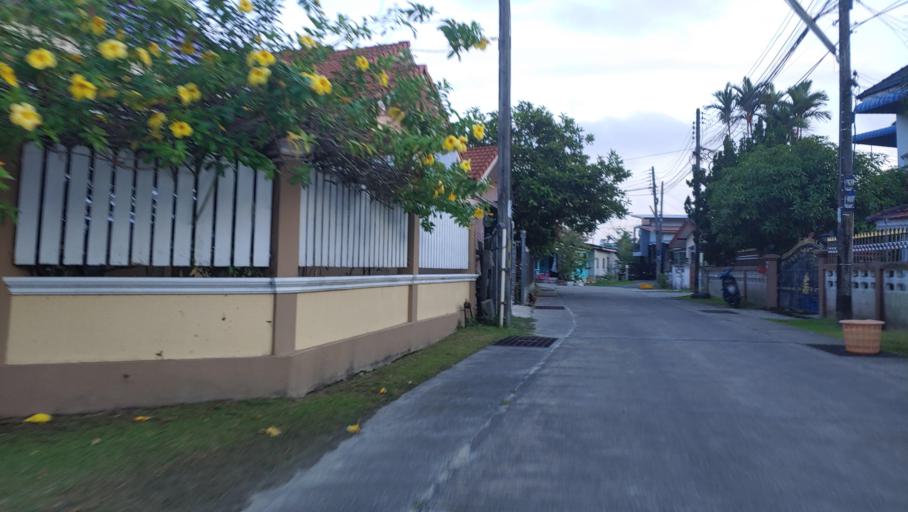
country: TH
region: Narathiwat
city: Narathiwat
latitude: 6.4401
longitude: 101.8177
